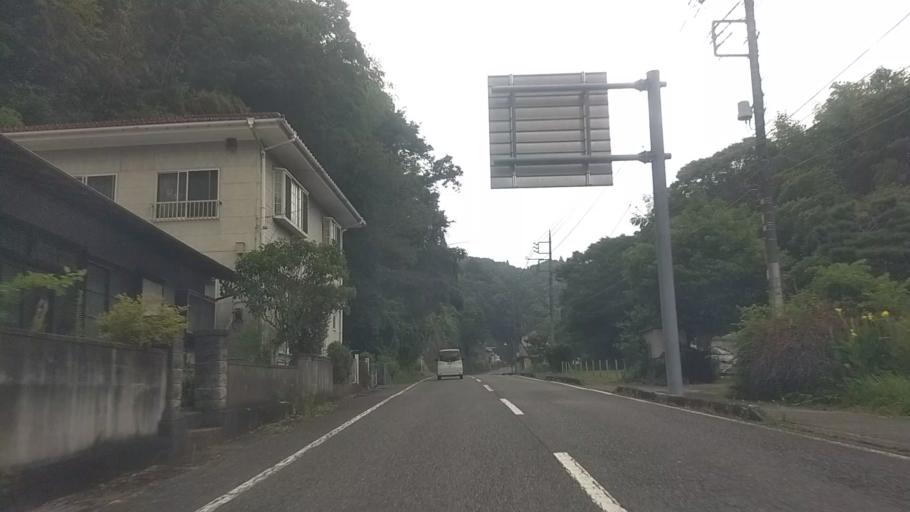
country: JP
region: Chiba
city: Kawaguchi
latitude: 35.2424
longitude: 140.1712
